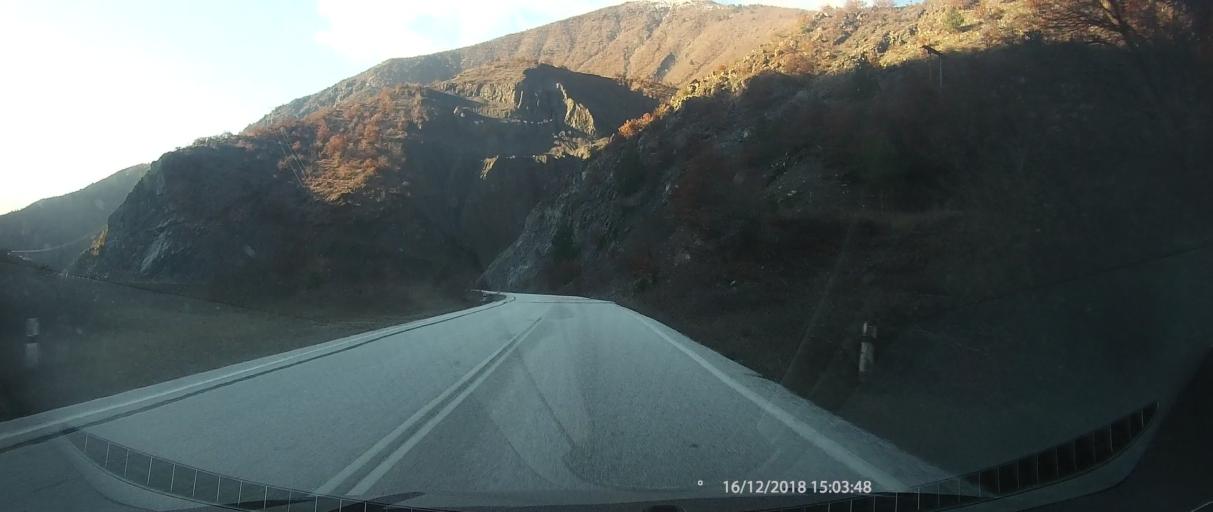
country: GR
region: West Macedonia
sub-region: Nomos Kastorias
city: Nestorio
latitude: 40.2281
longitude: 20.9773
